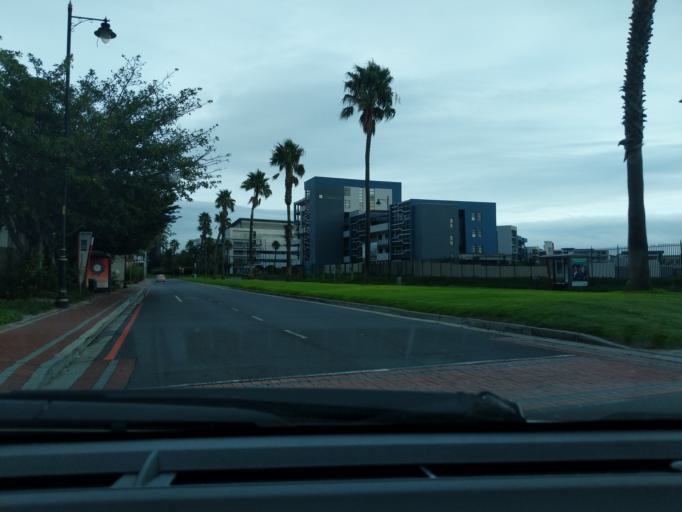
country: ZA
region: Western Cape
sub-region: City of Cape Town
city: Sunset Beach
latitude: -33.8841
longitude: 18.5210
